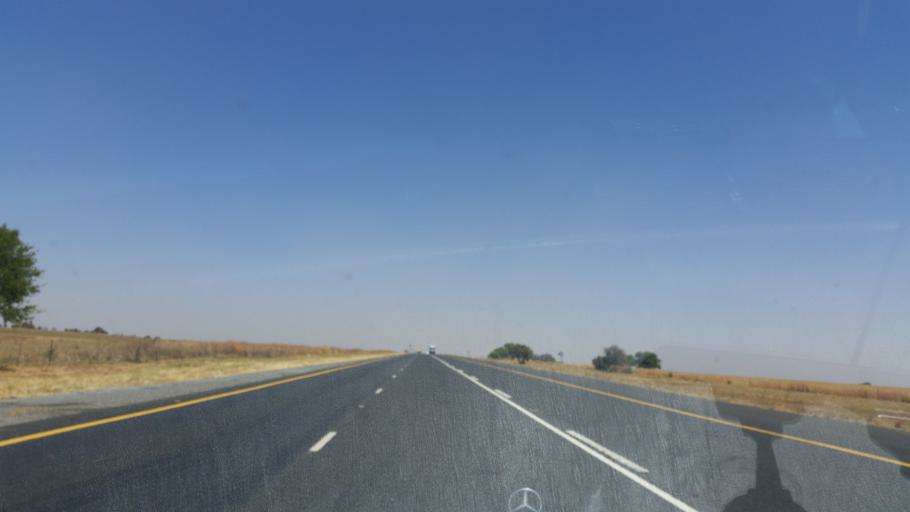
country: ZA
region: Orange Free State
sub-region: Lejweleputswa District Municipality
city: Winburg
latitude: -28.6431
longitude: 26.8866
